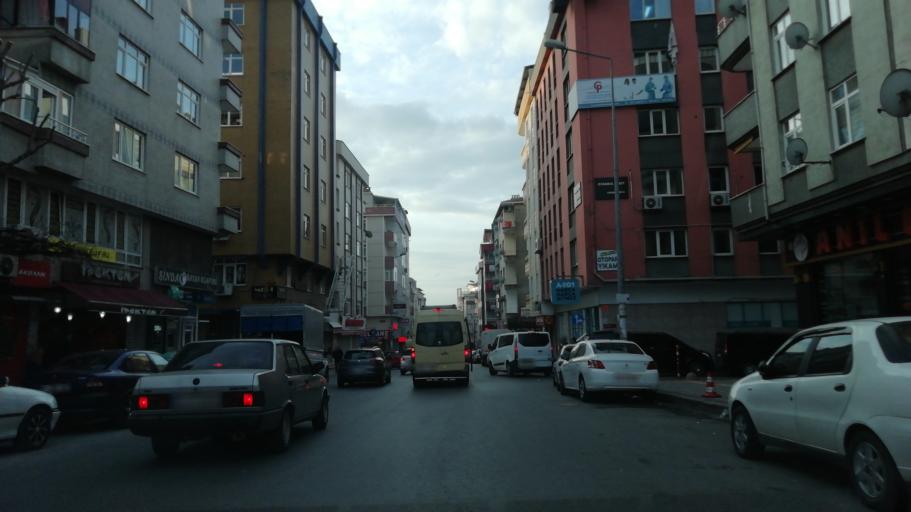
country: TR
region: Istanbul
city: Bahcelievler
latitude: 41.0014
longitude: 28.8302
